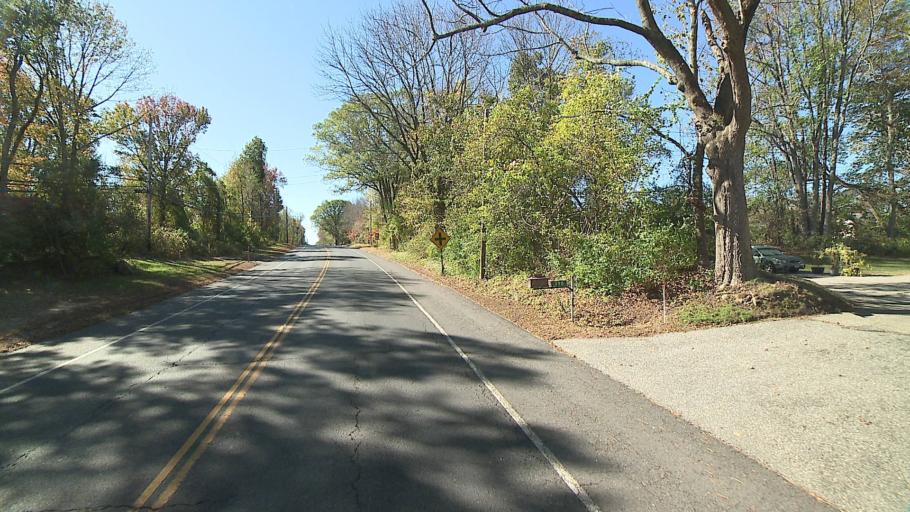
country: US
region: Connecticut
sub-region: Tolland County
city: Hebron
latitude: 41.6811
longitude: -72.3347
